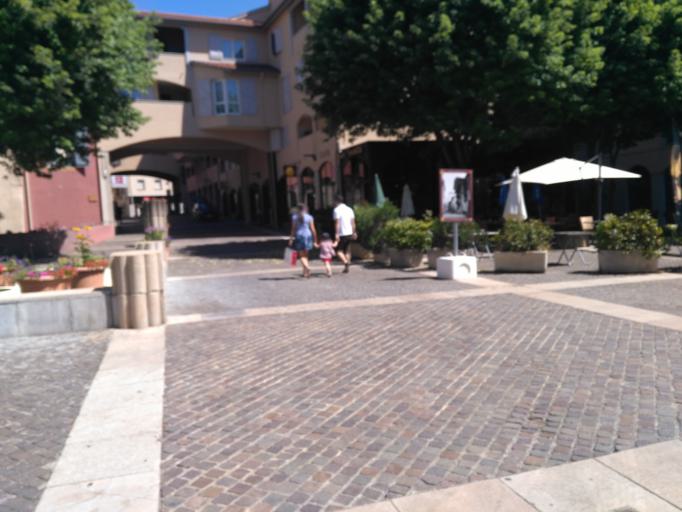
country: FR
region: Rhone-Alpes
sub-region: Departement du Rhone
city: Villefranche-sur-Saone
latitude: 45.9888
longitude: 4.7194
